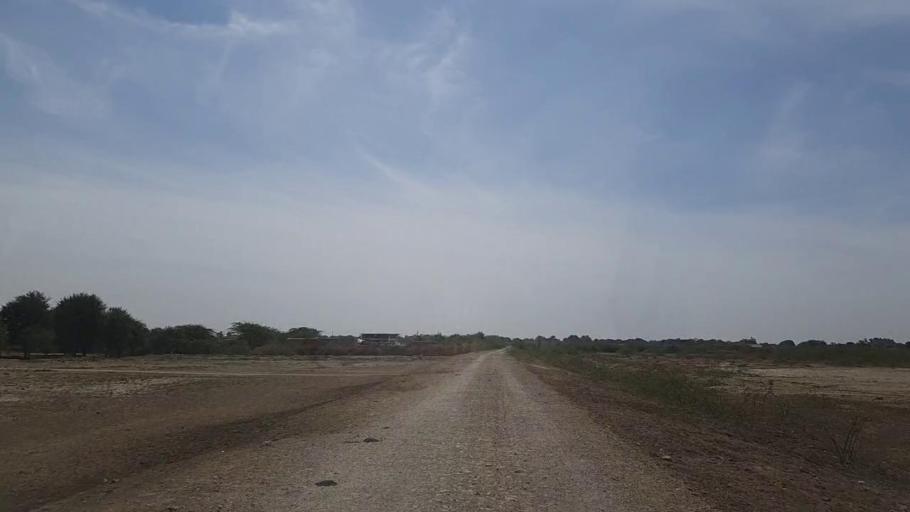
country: PK
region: Sindh
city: Samaro
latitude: 25.2700
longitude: 69.4785
